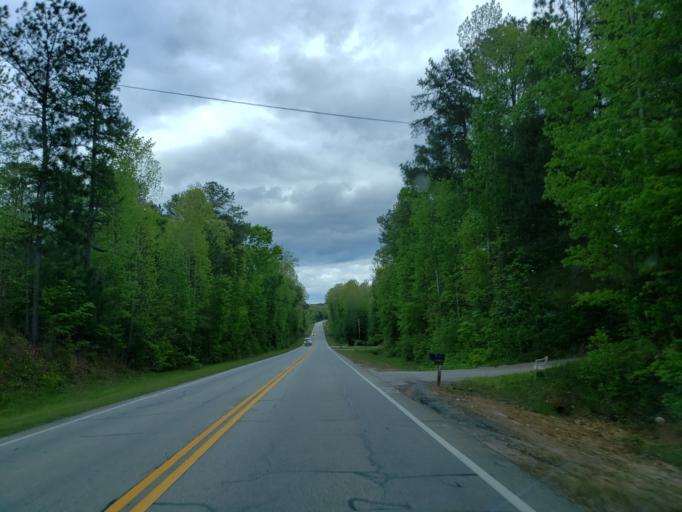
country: US
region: Georgia
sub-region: Carroll County
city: Temple
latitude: 33.8241
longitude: -85.0728
